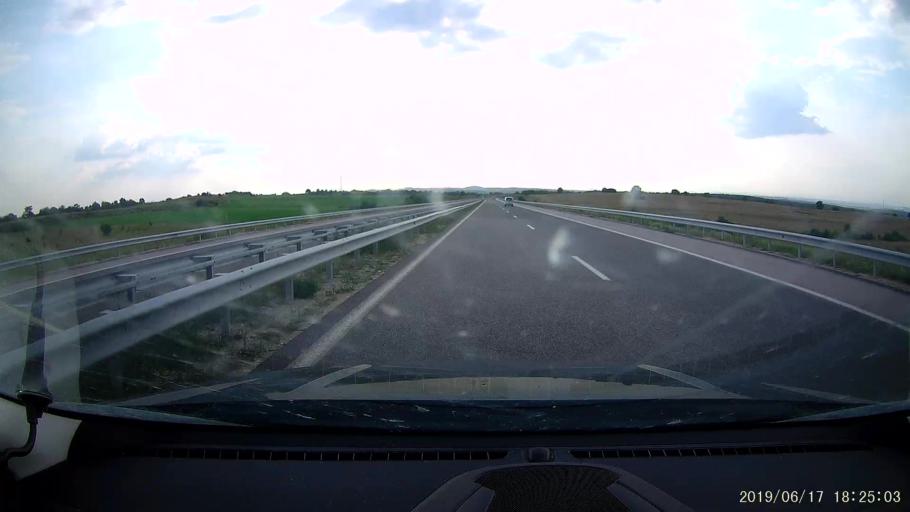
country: BG
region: Khaskovo
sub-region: Obshtina Dimitrovgrad
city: Dimitrovgrad
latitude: 41.9887
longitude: 25.6731
